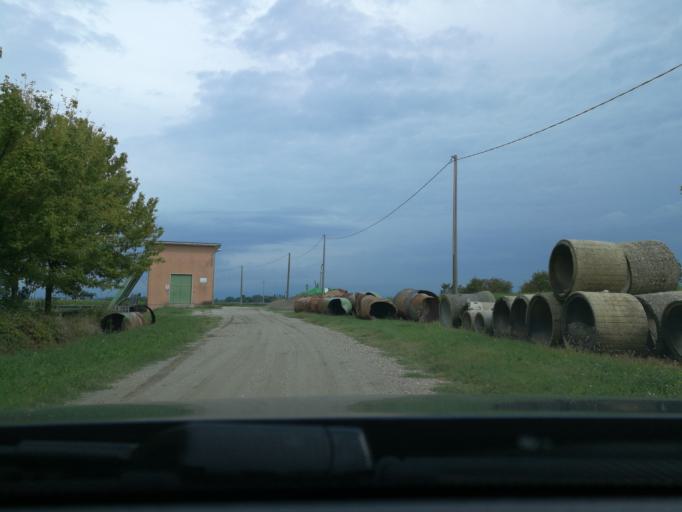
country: IT
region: Friuli Venezia Giulia
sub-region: Provincia di Udine
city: Pertegada
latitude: 45.7150
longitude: 13.0653
